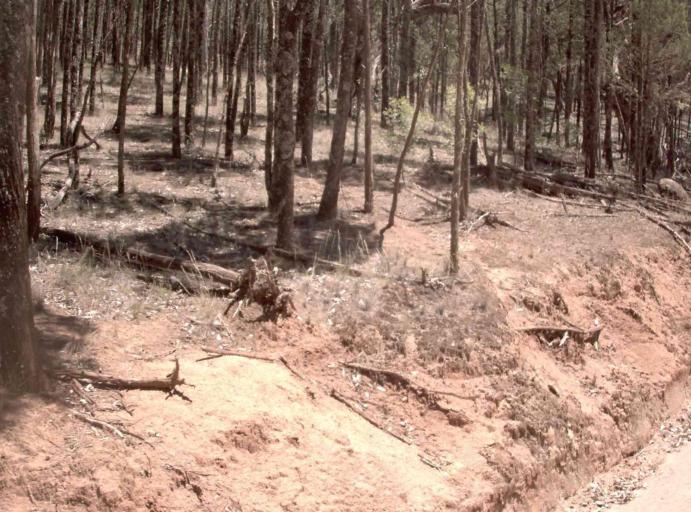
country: AU
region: New South Wales
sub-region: Snowy River
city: Jindabyne
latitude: -36.8990
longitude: 148.4179
